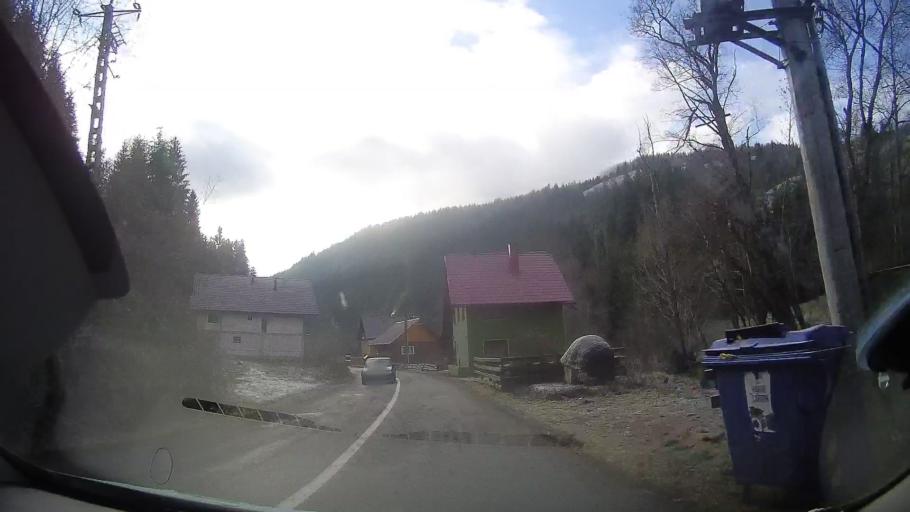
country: RO
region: Alba
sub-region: Comuna Horea
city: Horea
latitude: 46.4781
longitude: 22.9607
